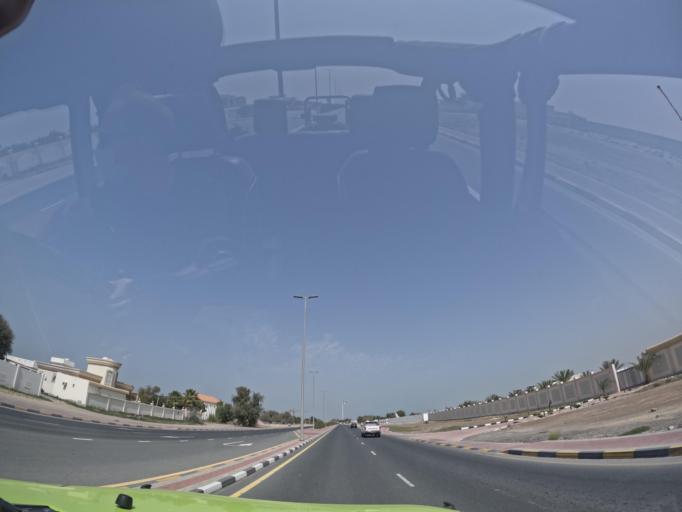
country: AE
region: Umm al Qaywayn
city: Umm al Qaywayn
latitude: 25.5550
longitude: 55.5610
